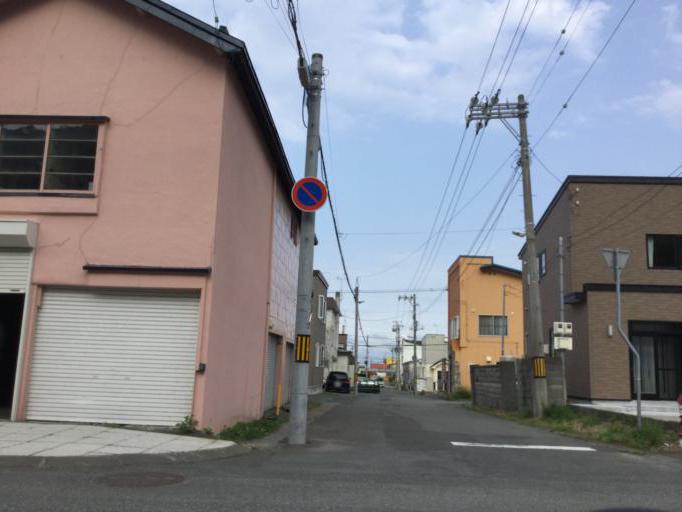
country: JP
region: Hokkaido
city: Wakkanai
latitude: 45.4118
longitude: 141.6739
